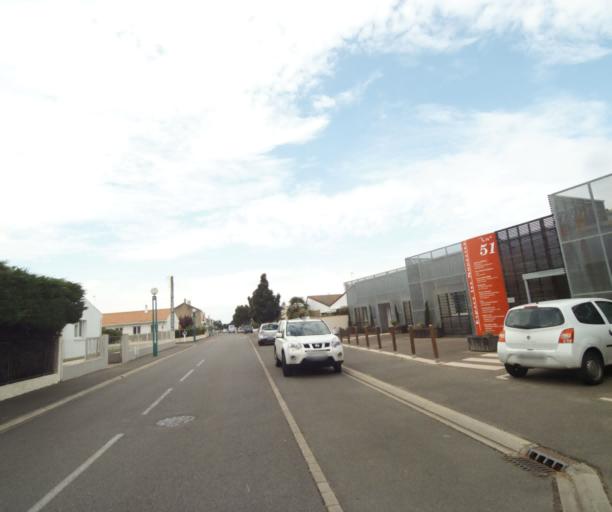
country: FR
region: Pays de la Loire
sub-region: Departement de la Vendee
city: Chateau-d'Olonne
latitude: 46.4966
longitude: -1.7579
